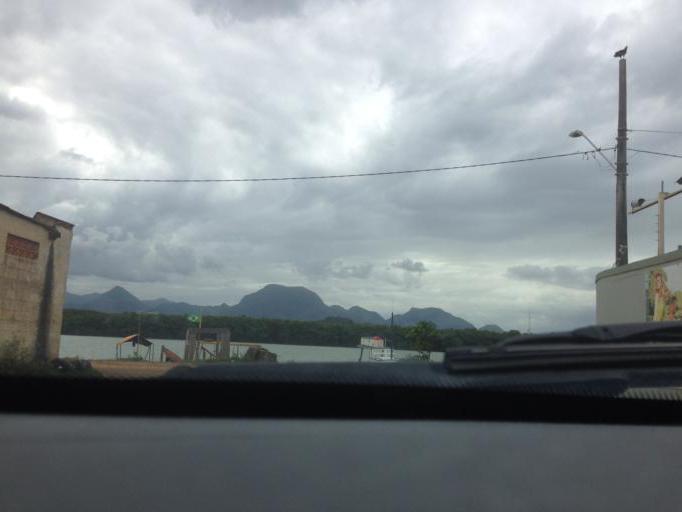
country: BR
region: Espirito Santo
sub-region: Guarapari
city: Guarapari
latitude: -20.6708
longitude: -40.5036
